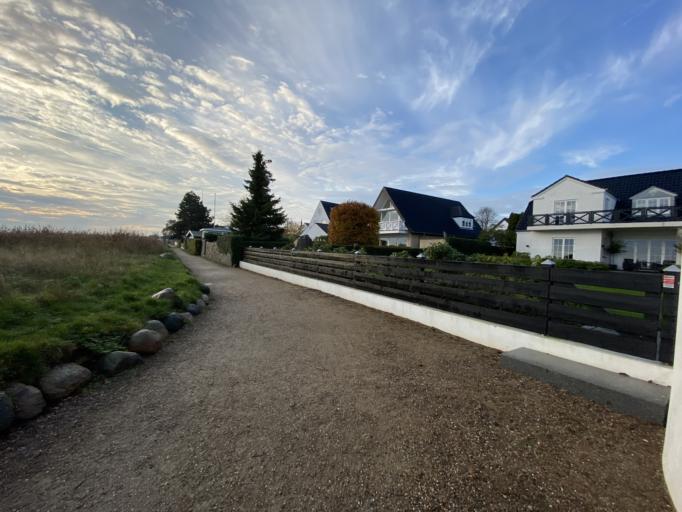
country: DK
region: Capital Region
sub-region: Dragor Kommune
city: Dragor
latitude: 55.6003
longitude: 12.6716
